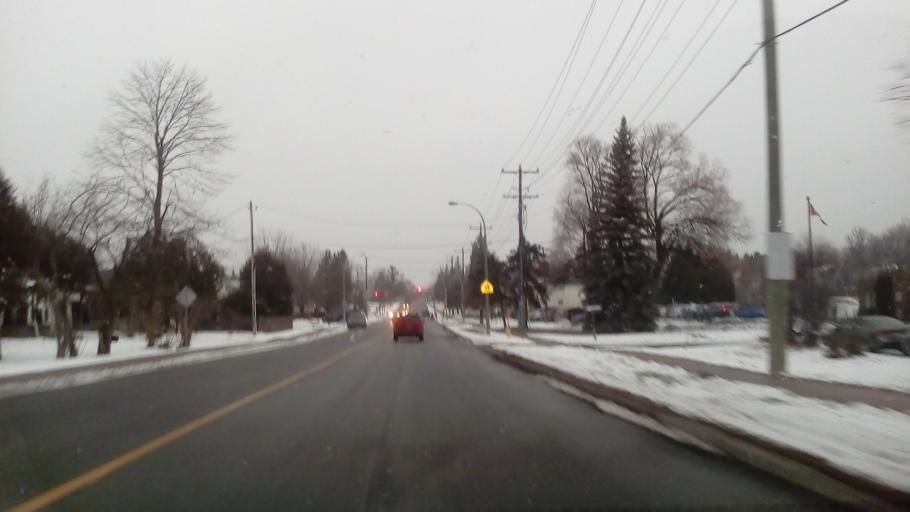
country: CA
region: Ontario
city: Ottawa
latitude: 45.4324
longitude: -75.5649
